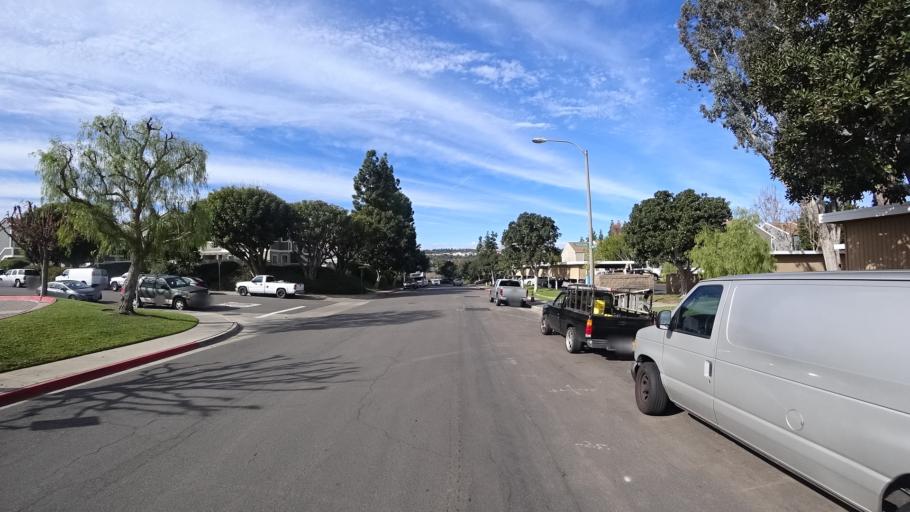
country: US
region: California
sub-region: Orange County
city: Aliso Viejo
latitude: 33.5735
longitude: -117.7105
